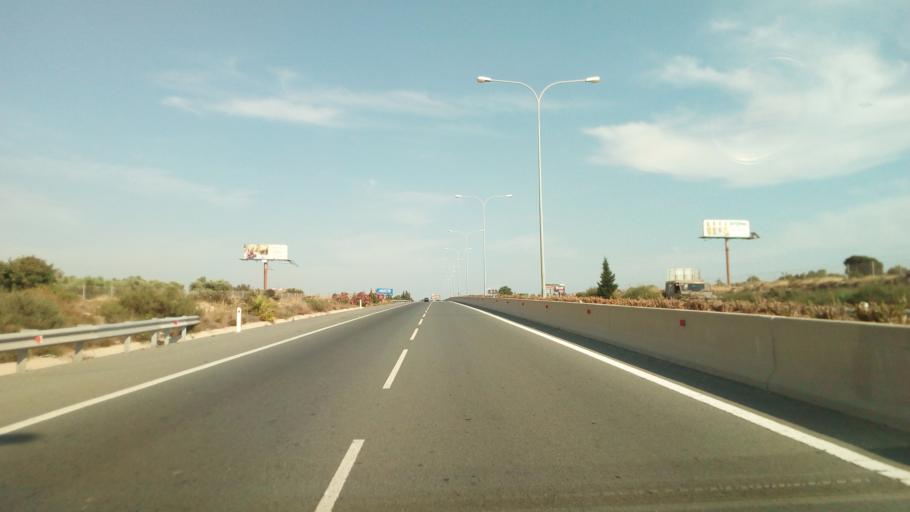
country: CY
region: Pafos
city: Paphos
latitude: 34.7742
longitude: 32.4617
